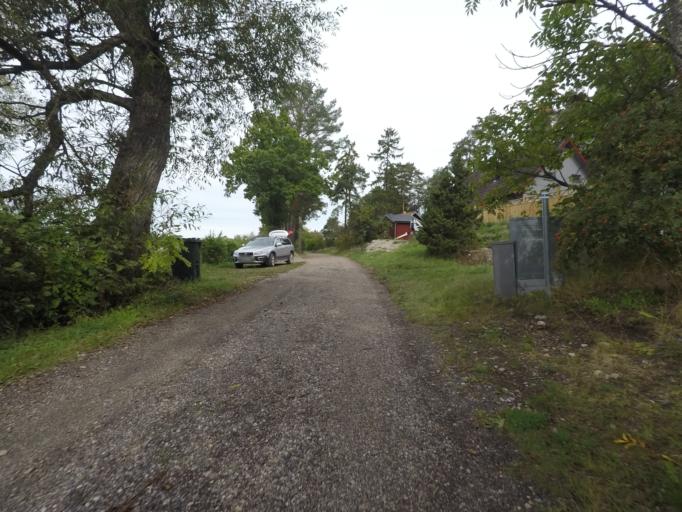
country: SE
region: Vaestmanland
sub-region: Kungsors Kommun
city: Kungsoer
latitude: 59.4672
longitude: 16.0713
